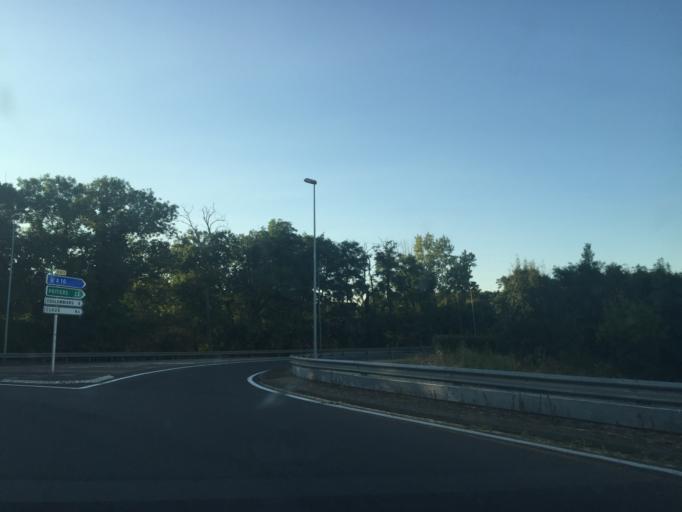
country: FR
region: Poitou-Charentes
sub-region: Departement de la Vienne
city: Lusignan
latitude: 46.4477
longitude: 0.1378
